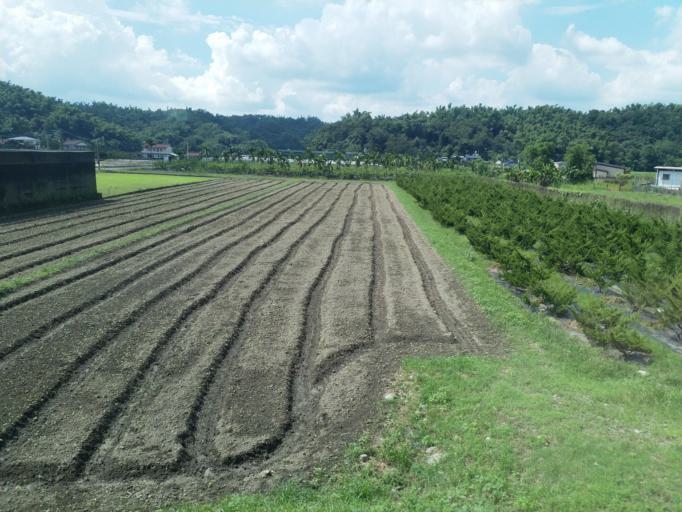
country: TW
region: Taiwan
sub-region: Pingtung
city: Pingtung
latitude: 22.8939
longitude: 120.5797
